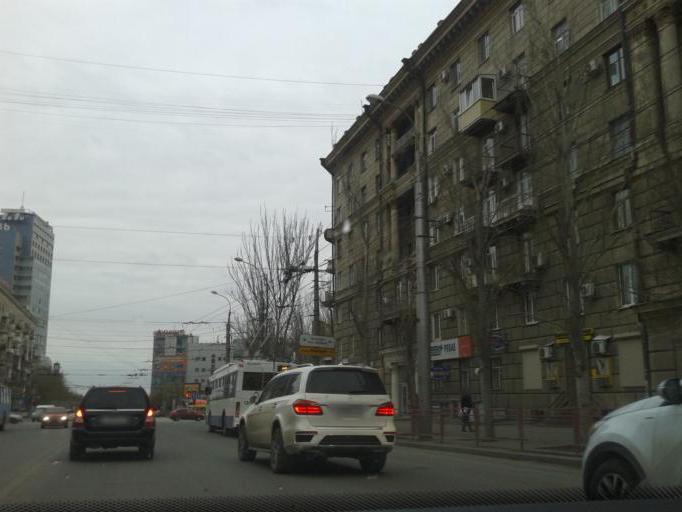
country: RU
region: Volgograd
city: Volgograd
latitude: 48.7099
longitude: 44.5194
